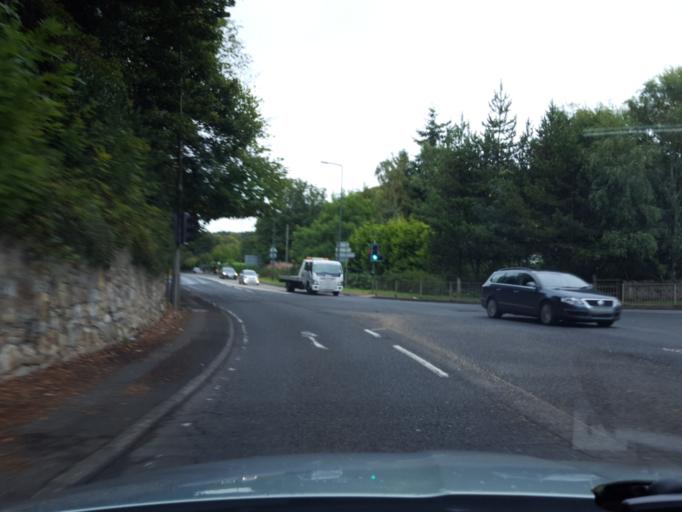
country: GB
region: Scotland
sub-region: Midlothian
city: Bonnyrigg
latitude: 55.8831
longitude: -3.1255
